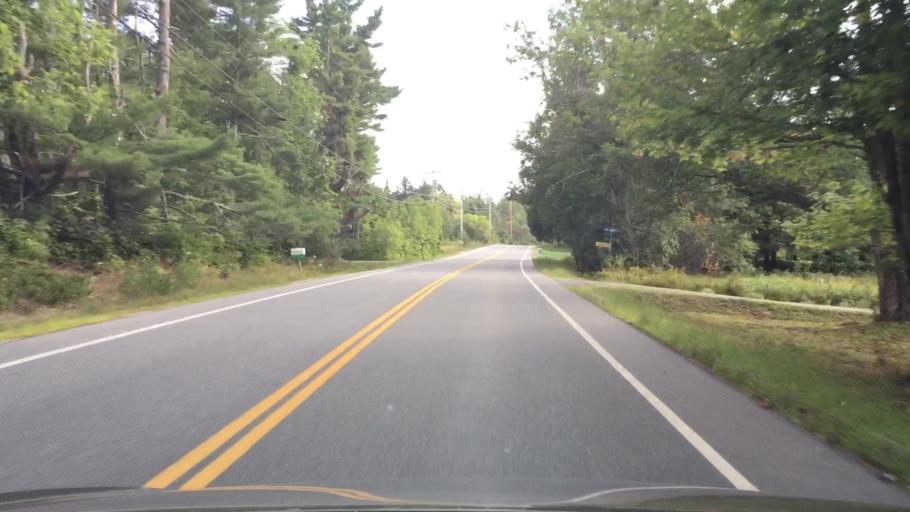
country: US
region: Maine
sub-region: Hancock County
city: Castine
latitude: 44.4442
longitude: -68.7867
